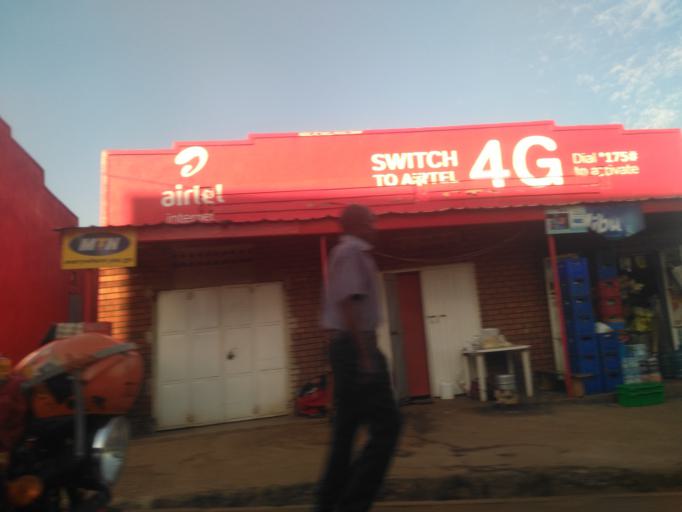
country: UG
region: Central Region
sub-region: Kampala District
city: Kampala
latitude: 0.3104
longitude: 32.6001
